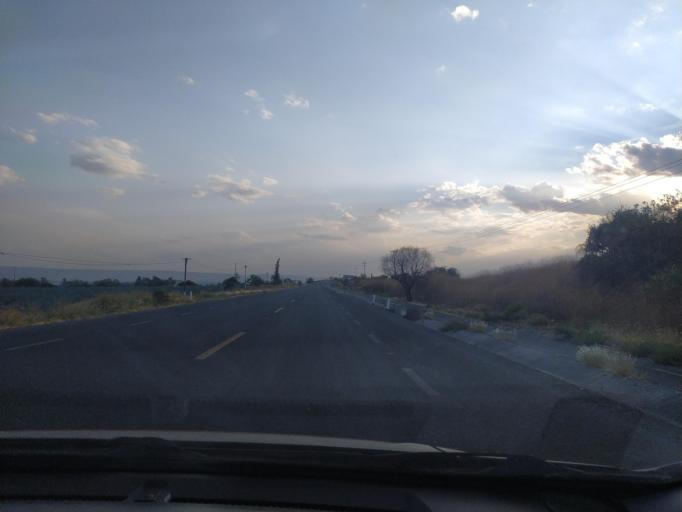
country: MX
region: Guanajuato
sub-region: San Francisco del Rincon
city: San Ignacio de Hidalgo
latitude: 20.8954
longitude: -101.9312
